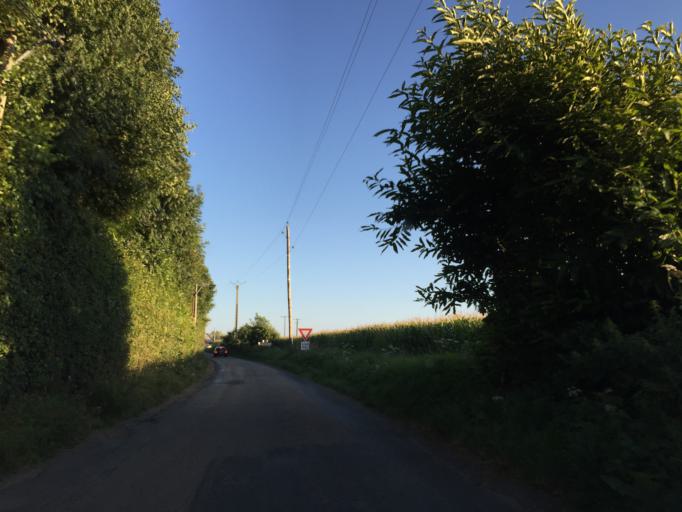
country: FR
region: Lower Normandy
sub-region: Departement du Calvados
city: Equemauville
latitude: 49.3988
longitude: 0.2051
